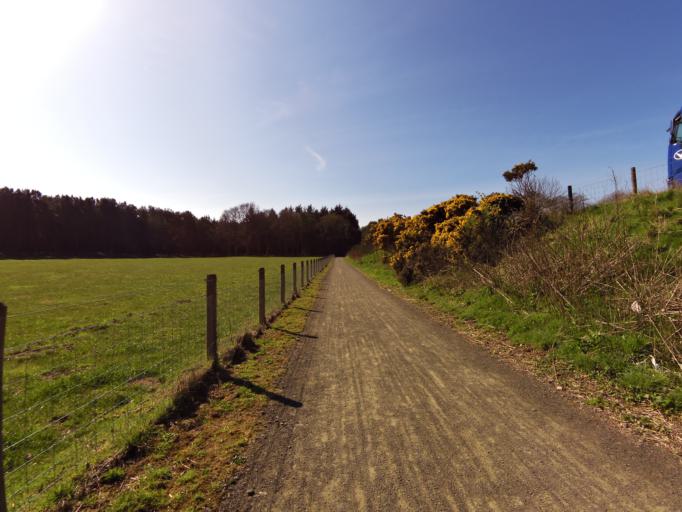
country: GB
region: Scotland
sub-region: Angus
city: Montrose
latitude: 56.7432
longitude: -2.4529
